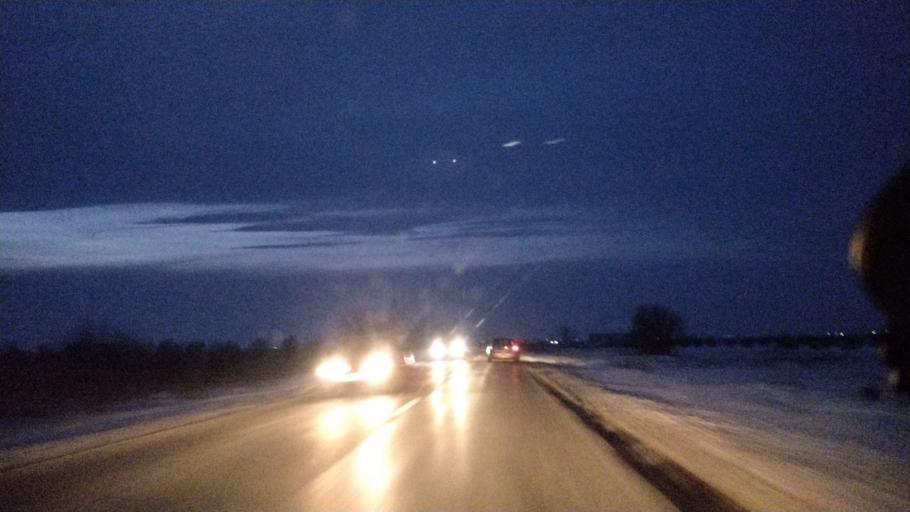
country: RO
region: Vrancea
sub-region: Comuna Milcovul
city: Milcovul
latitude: 45.6686
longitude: 27.2638
